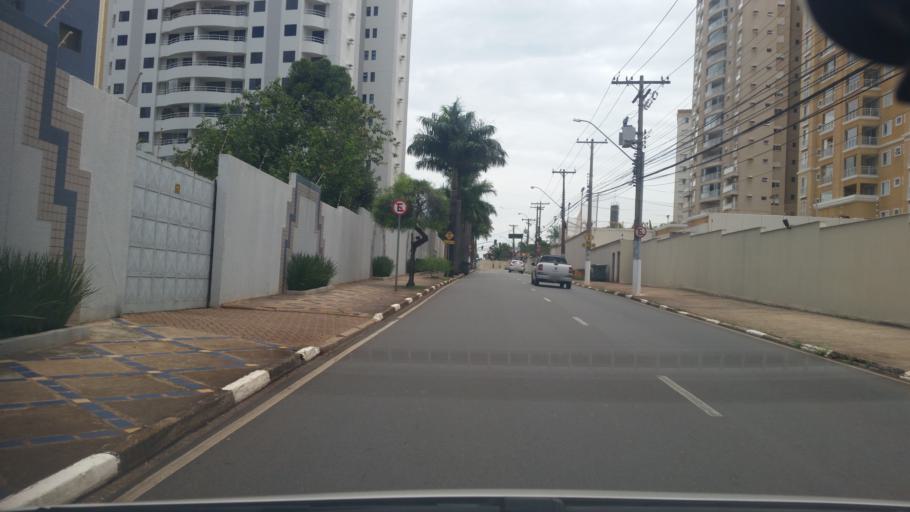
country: BR
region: Sao Paulo
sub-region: Campinas
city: Campinas
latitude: -22.8529
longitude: -47.0535
